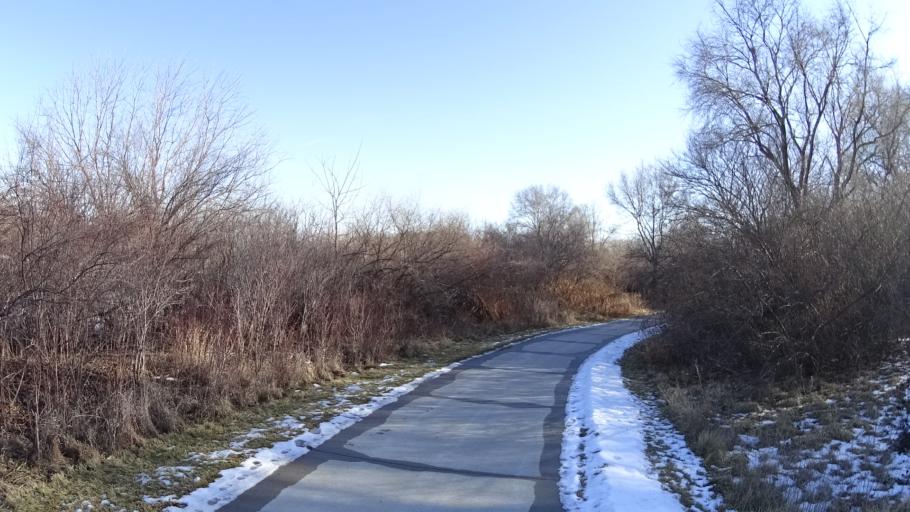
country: US
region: Nebraska
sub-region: Douglas County
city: Bennington
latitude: 41.3129
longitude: -96.1275
